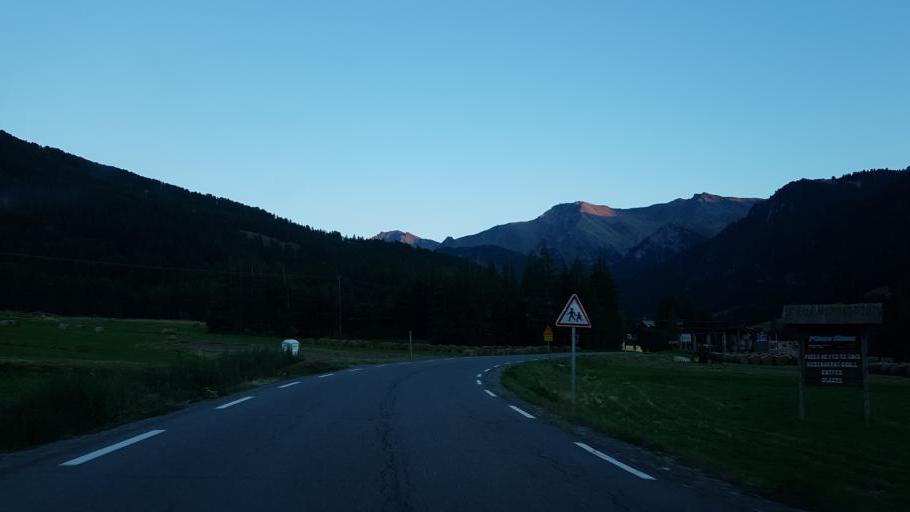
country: FR
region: Provence-Alpes-Cote d'Azur
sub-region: Departement des Hautes-Alpes
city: Guillestre
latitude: 44.7253
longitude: 6.8471
